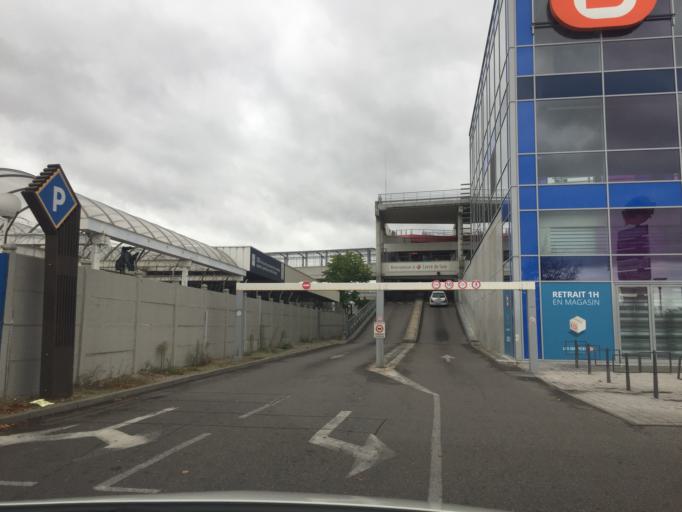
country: FR
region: Rhone-Alpes
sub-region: Departement du Rhone
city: Vaulx-en-Velin
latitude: 45.7653
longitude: 4.9235
